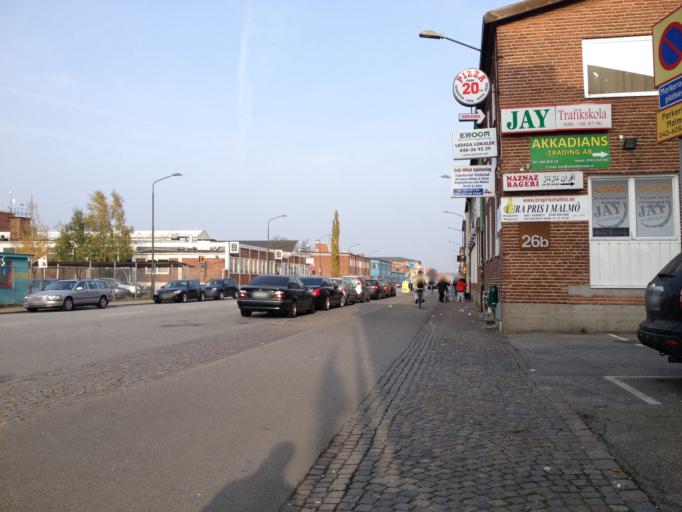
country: SE
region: Skane
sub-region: Malmo
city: Malmoe
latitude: 55.5837
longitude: 13.0262
